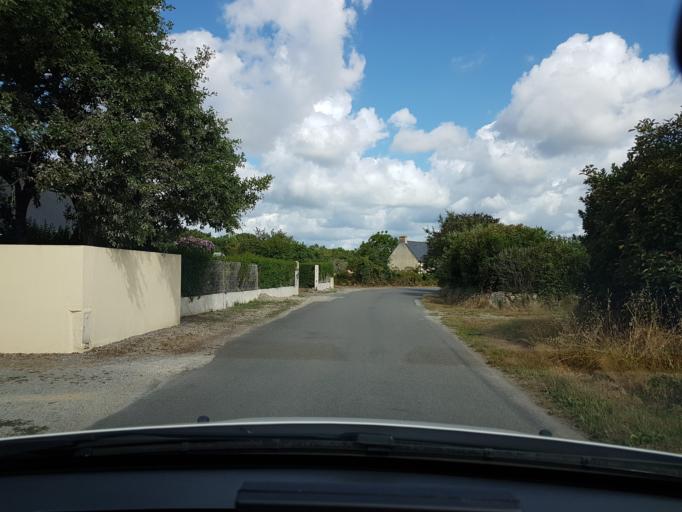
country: FR
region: Brittany
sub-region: Departement du Morbihan
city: Sainte-Helene
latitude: 47.7073
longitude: -3.1934
